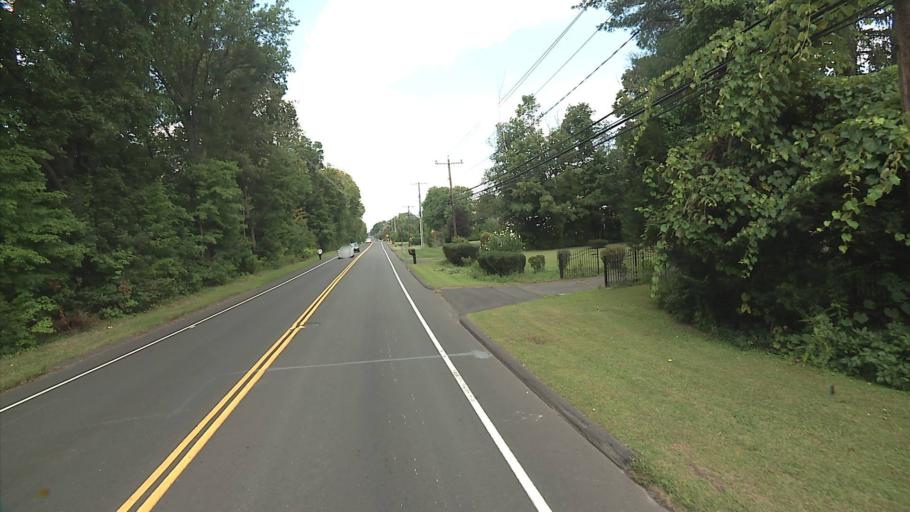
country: US
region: Connecticut
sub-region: Hartford County
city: Blue Hills
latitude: 41.8023
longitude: -72.7259
